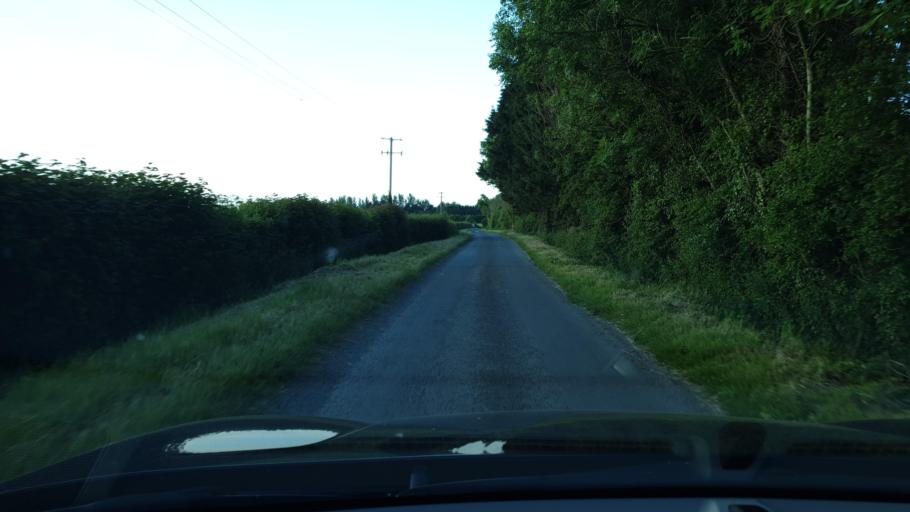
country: IE
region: Leinster
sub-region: Fingal County
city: Blanchardstown
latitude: 53.4424
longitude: -6.3948
